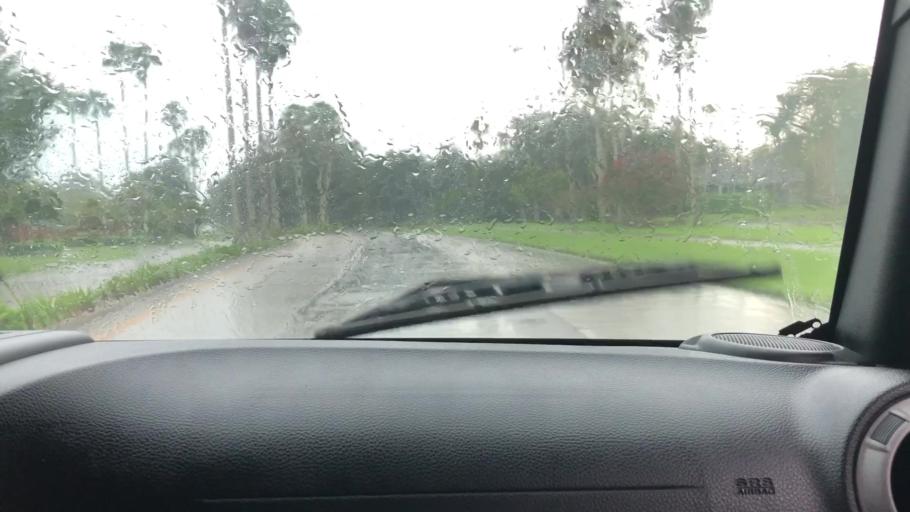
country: US
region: Florida
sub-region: Hillsborough County
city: University
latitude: 28.1033
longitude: -82.4022
